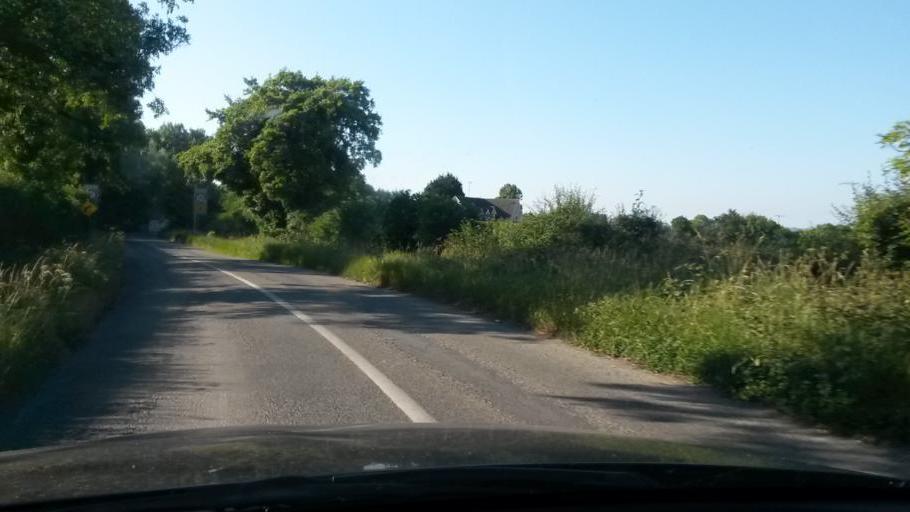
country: IE
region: Leinster
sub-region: Dublin City
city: Finglas
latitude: 53.4720
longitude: -6.3194
